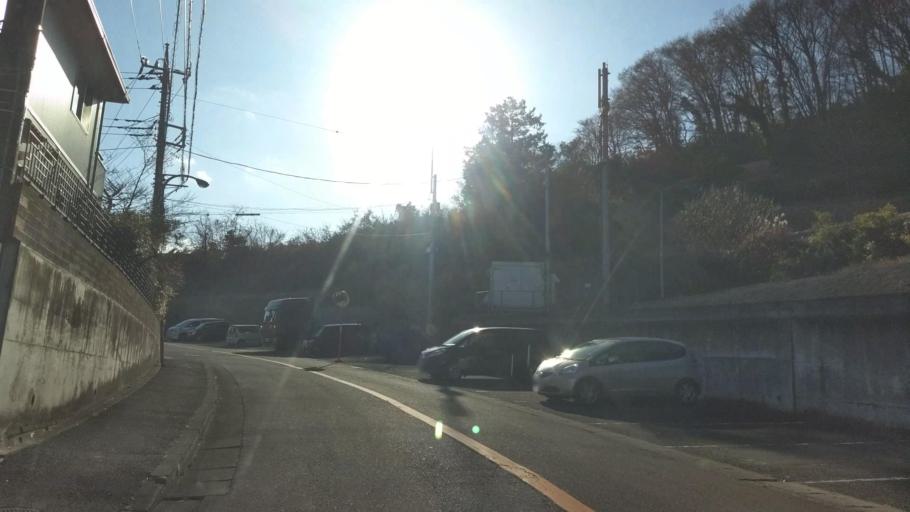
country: JP
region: Kanagawa
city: Hadano
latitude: 35.3673
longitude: 139.2516
